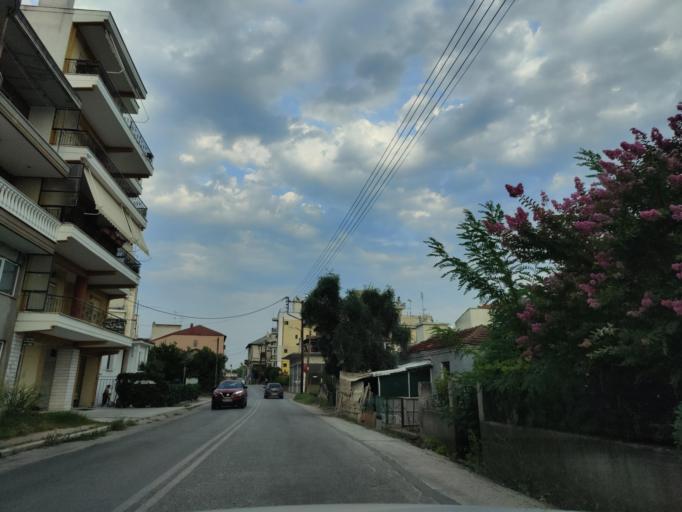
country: GR
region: East Macedonia and Thrace
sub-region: Nomos Dramas
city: Drama
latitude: 41.1498
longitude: 24.1365
